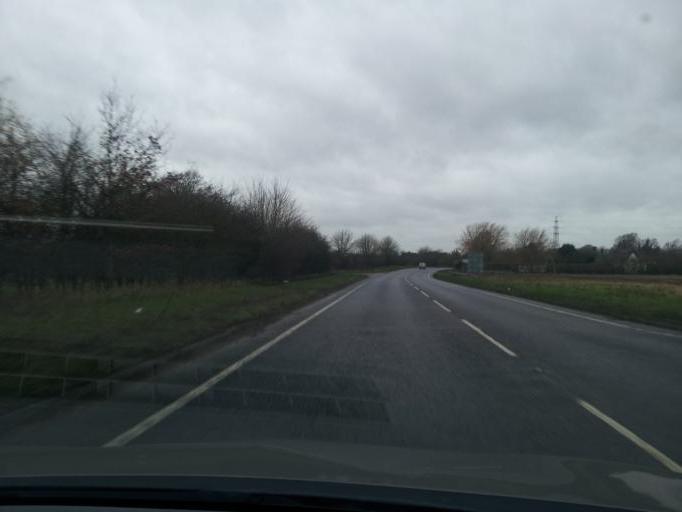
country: GB
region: England
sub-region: Norfolk
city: Diss
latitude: 52.3554
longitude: 1.1029
